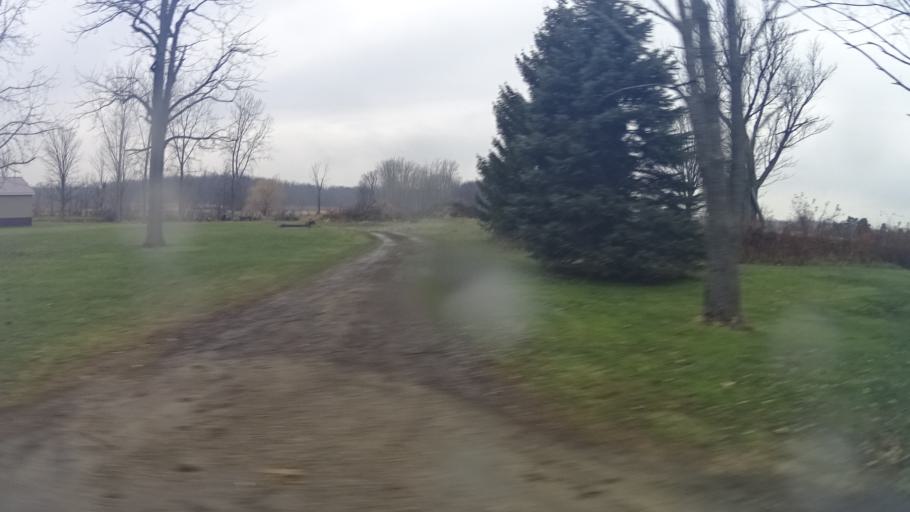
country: US
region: Ohio
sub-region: Lorain County
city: Lagrange
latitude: 41.2184
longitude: -82.1579
